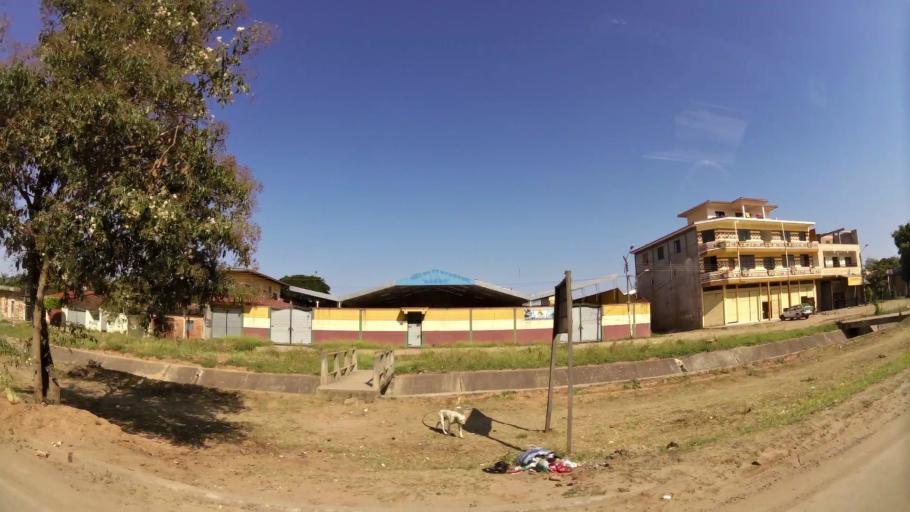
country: BO
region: Santa Cruz
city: Cotoca
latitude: -17.8150
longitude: -63.1124
